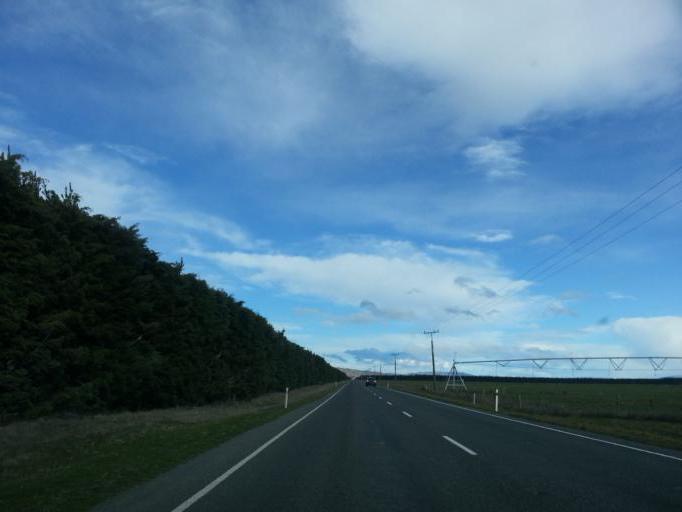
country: NZ
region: Canterbury
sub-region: Hurunui District
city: Amberley
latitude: -42.8050
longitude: 172.8234
